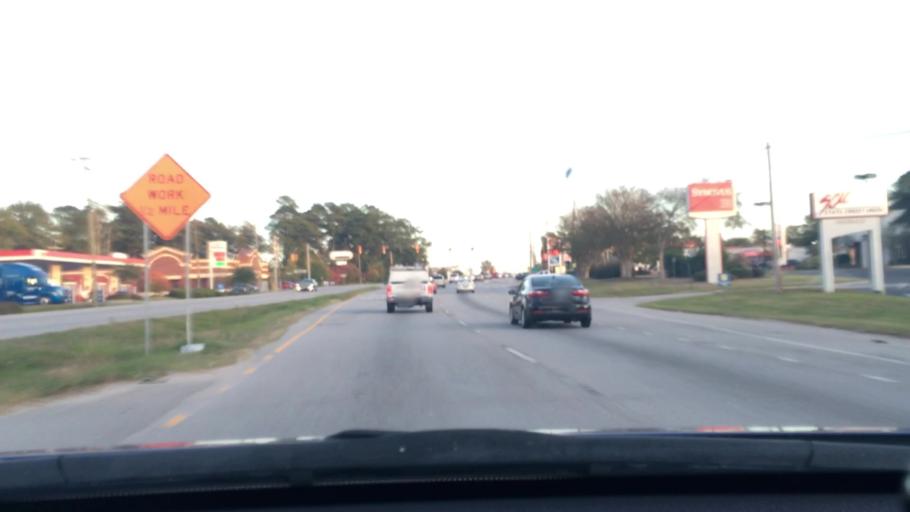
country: US
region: South Carolina
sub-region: Richland County
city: Hopkins
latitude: 33.9554
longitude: -80.9268
